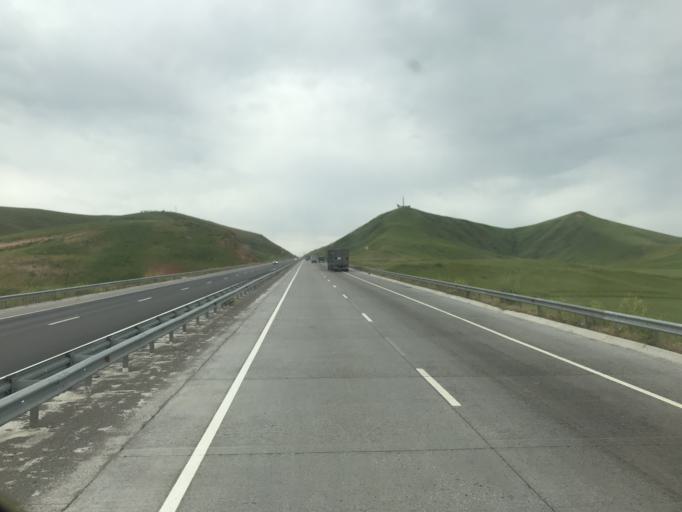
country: KZ
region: Ongtustik Qazaqstan
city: Qazyqurt
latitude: 42.0113
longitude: 69.4722
